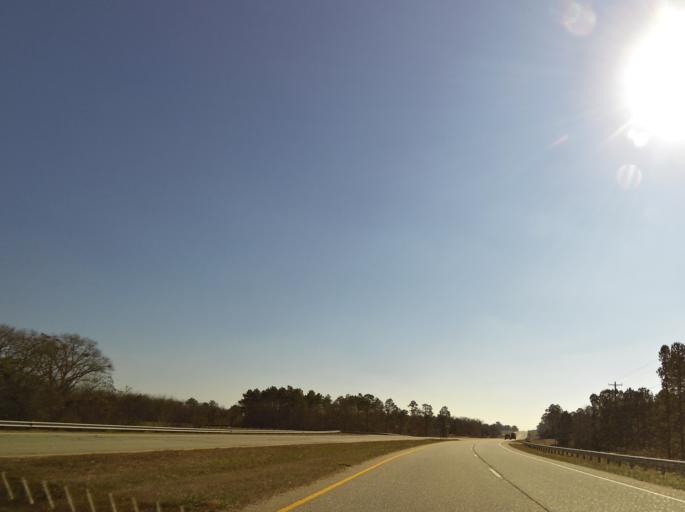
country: US
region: Georgia
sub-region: Pulaski County
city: Hawkinsville
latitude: 32.3088
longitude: -83.5073
